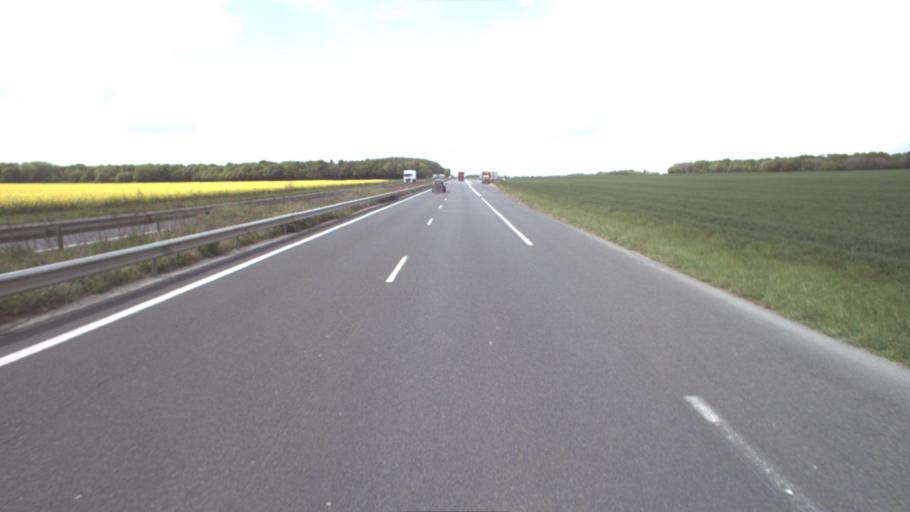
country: FR
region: Ile-de-France
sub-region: Departement de Seine-et-Marne
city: Rozay-en-Brie
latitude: 48.6900
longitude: 2.9215
